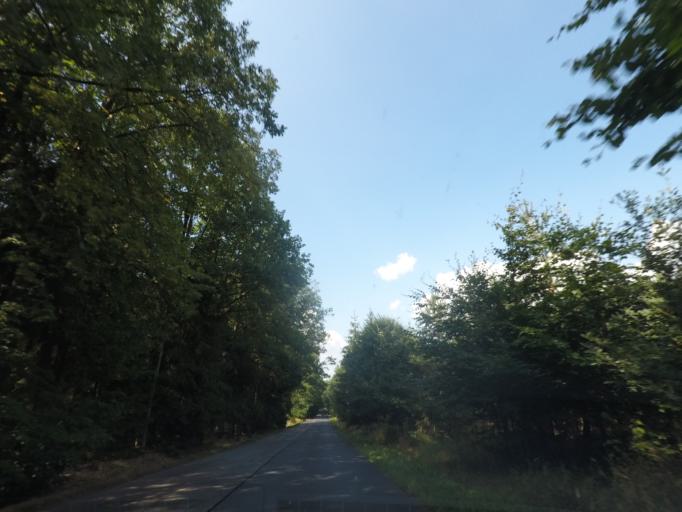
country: CZ
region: Pardubicky
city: Horni Jeleni
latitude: 50.0264
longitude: 16.0817
